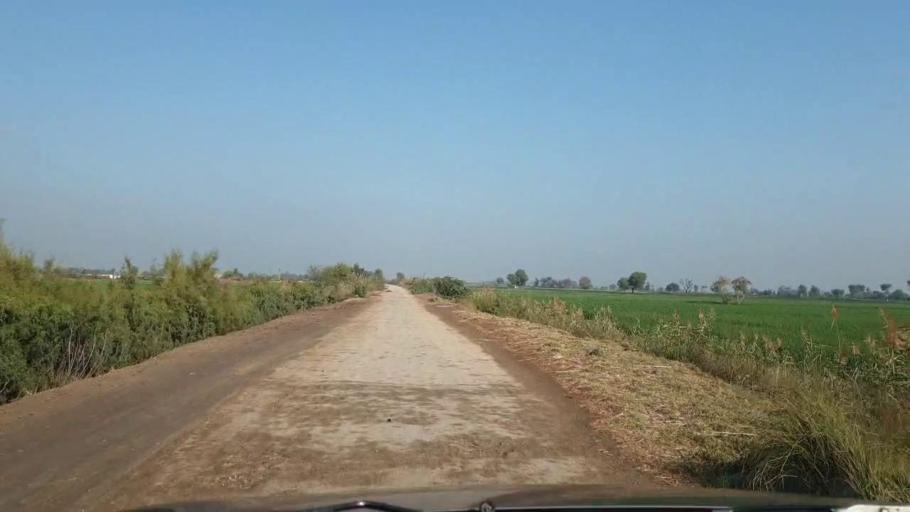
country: PK
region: Sindh
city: Sinjhoro
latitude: 26.0592
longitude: 68.7881
